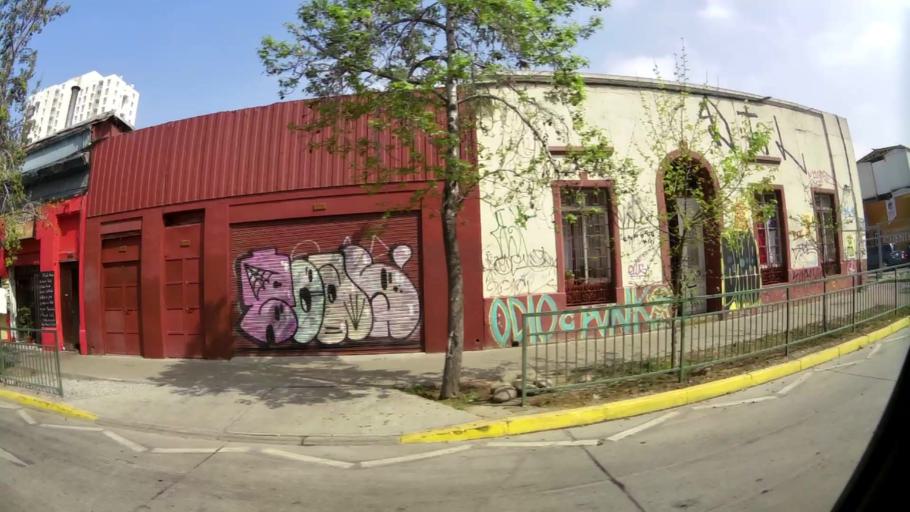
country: CL
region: Santiago Metropolitan
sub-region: Provincia de Santiago
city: Santiago
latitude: -33.4571
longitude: -70.6436
